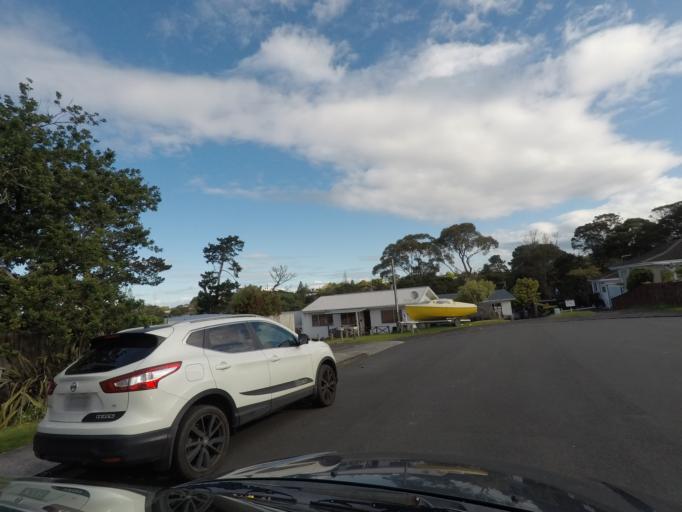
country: NZ
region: Auckland
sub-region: Auckland
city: Rosebank
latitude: -36.8805
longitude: 174.6549
